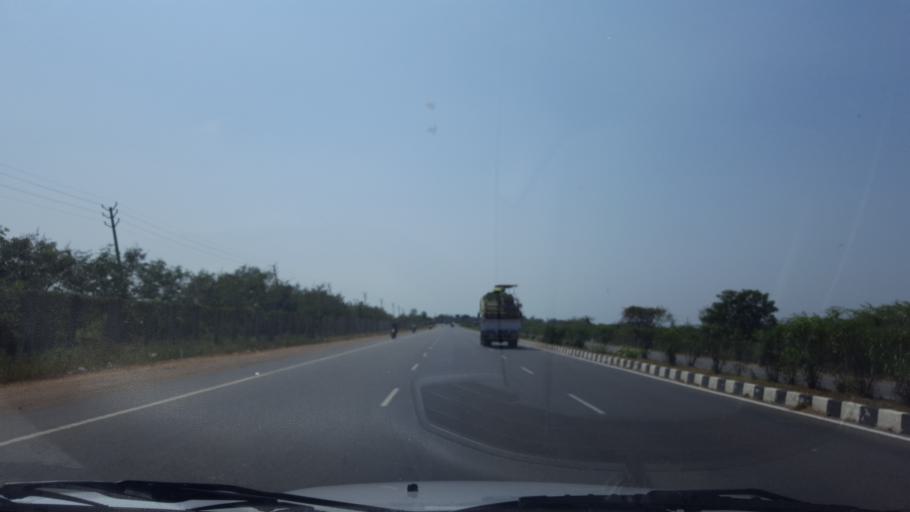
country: IN
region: Andhra Pradesh
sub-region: Prakasam
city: Addanki
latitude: 15.7490
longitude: 80.0284
